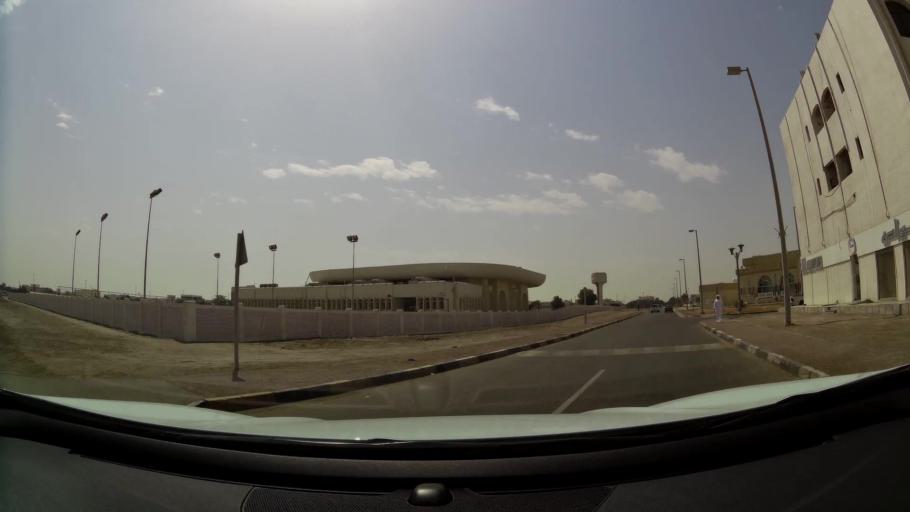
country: AE
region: Abu Dhabi
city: Abu Dhabi
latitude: 24.2957
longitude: 54.6404
